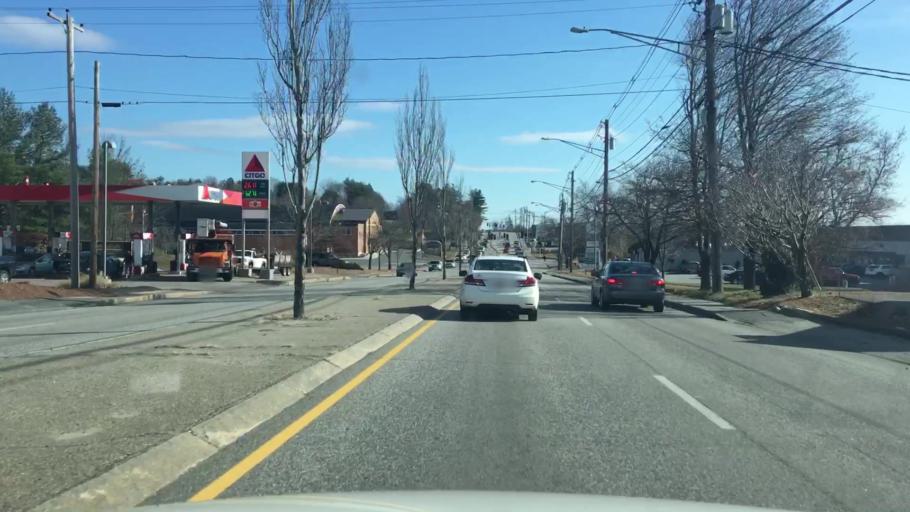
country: US
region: Maine
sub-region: Kennebec County
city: Augusta
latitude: 44.3139
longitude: -69.7992
